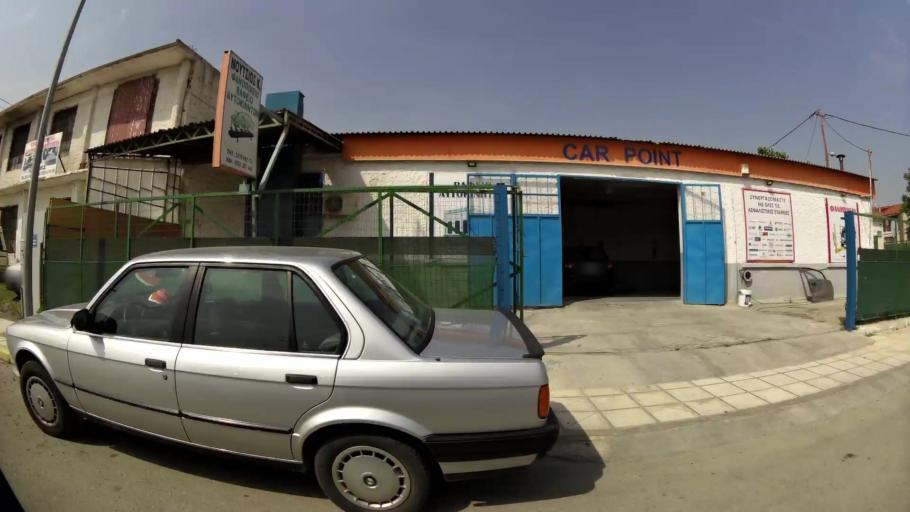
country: GR
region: Central Macedonia
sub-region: Nomos Thessalonikis
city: Efkarpia
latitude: 40.6854
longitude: 22.9451
